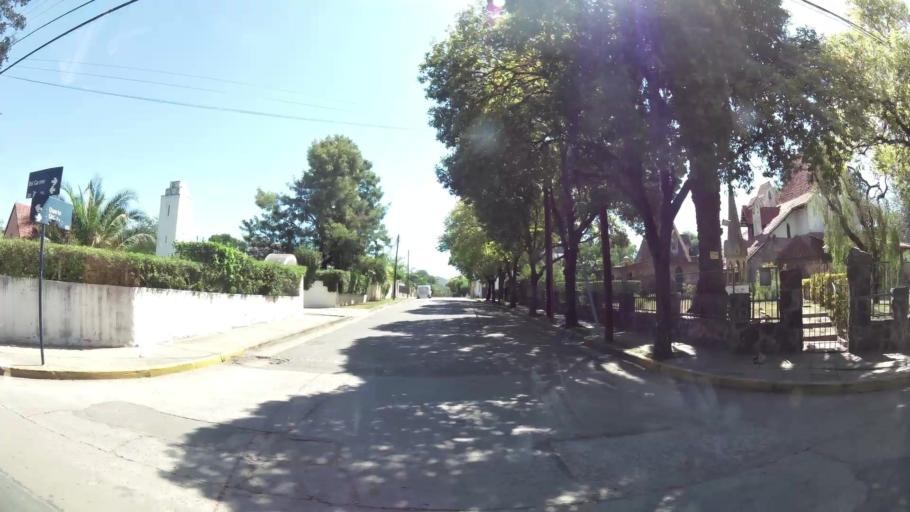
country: AR
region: Cordoba
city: Villa Allende
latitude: -31.2913
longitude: -64.2973
